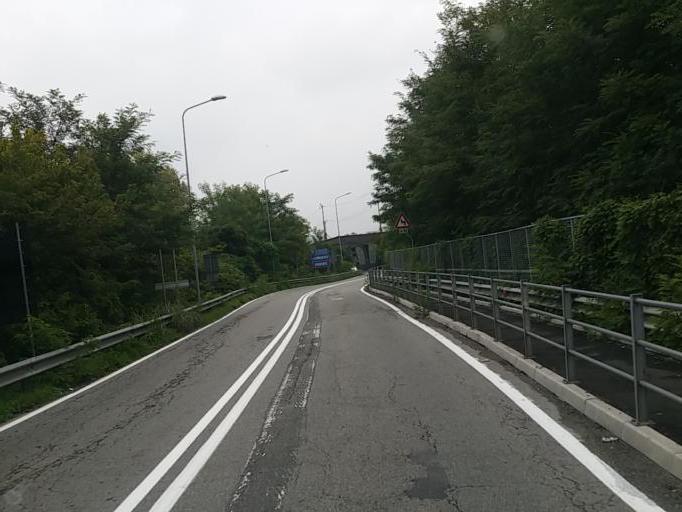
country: IT
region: Piedmont
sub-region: Provincia di Novara
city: Castelletto Sopra Ticino
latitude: 45.7205
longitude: 8.6263
